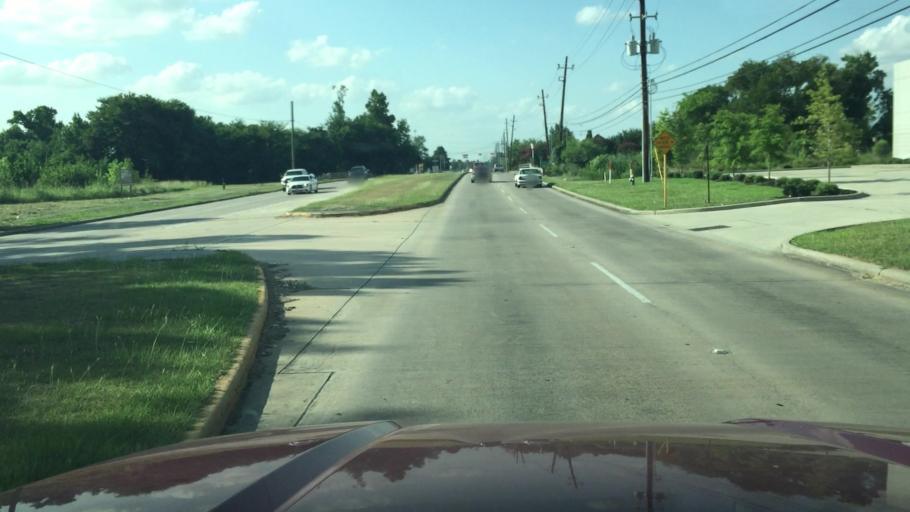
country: US
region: Texas
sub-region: Harris County
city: Hudson
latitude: 29.9474
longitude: -95.4981
